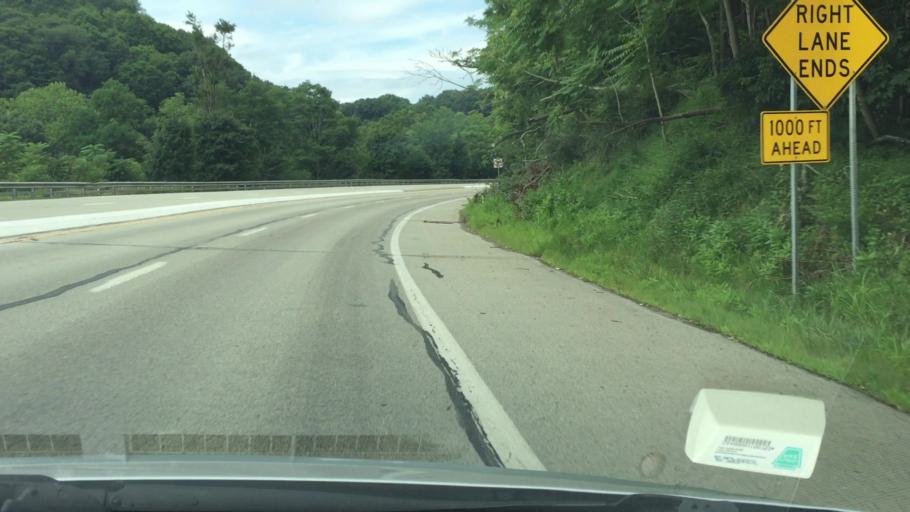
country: US
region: Pennsylvania
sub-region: Westmoreland County
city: New Kensington
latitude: 40.5749
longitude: -79.7435
